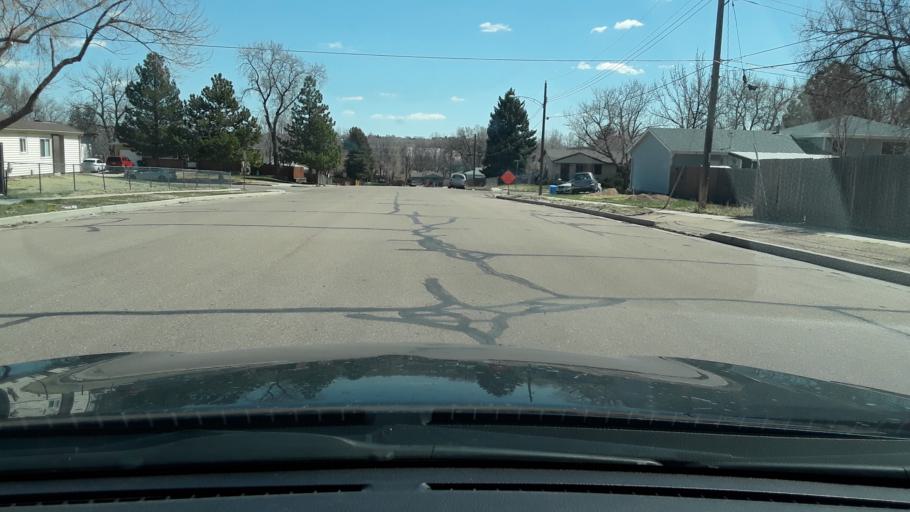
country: US
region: Colorado
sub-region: El Paso County
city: Colorado Springs
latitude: 38.8435
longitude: -104.7705
